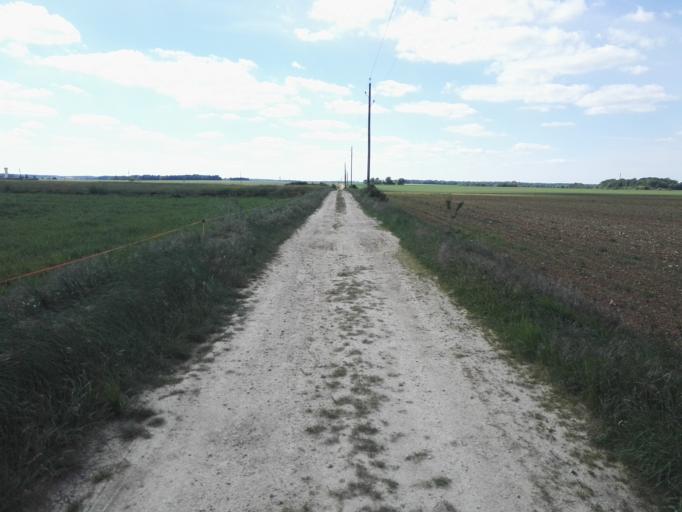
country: FR
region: Haute-Normandie
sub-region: Departement de l'Eure
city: Pacy-sur-Eure
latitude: 48.9925
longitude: 1.3628
